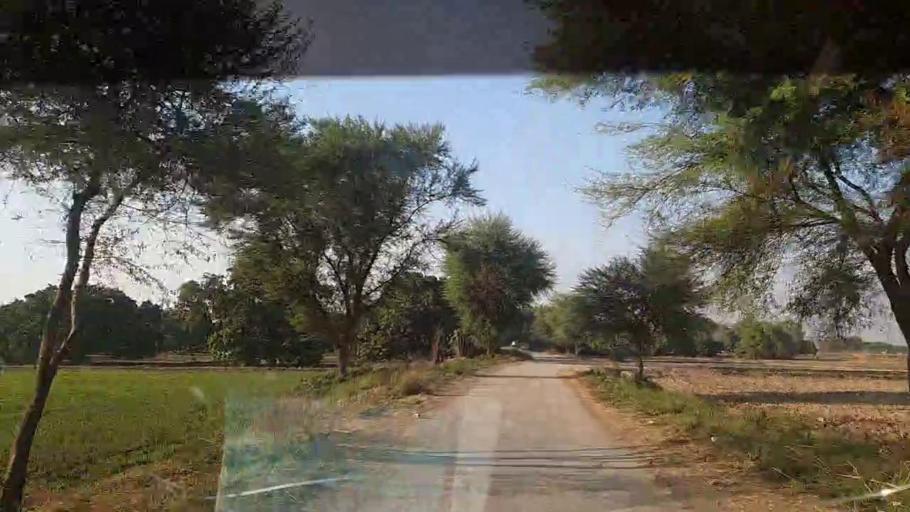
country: PK
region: Sindh
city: Sobhadero
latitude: 27.3042
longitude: 68.4228
